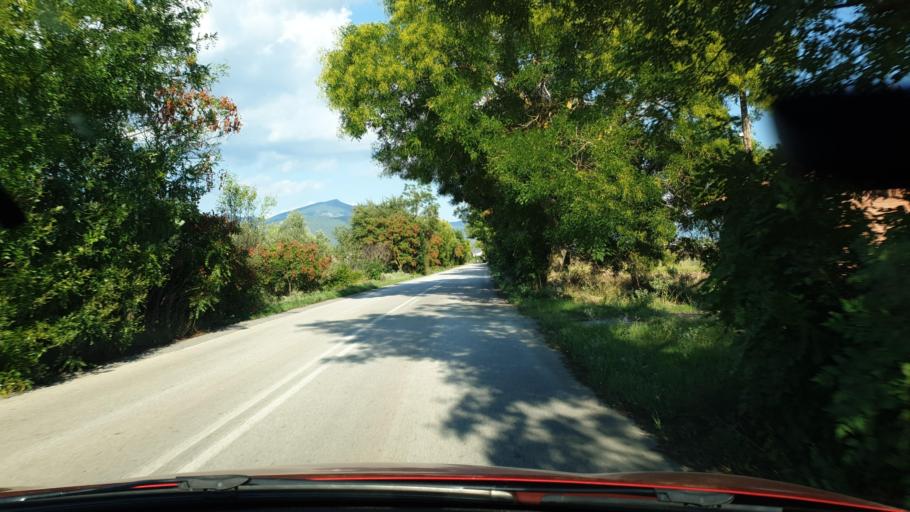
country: GR
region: Central Macedonia
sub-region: Nomos Thessalonikis
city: Souroti
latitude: 40.4761
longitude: 23.1029
